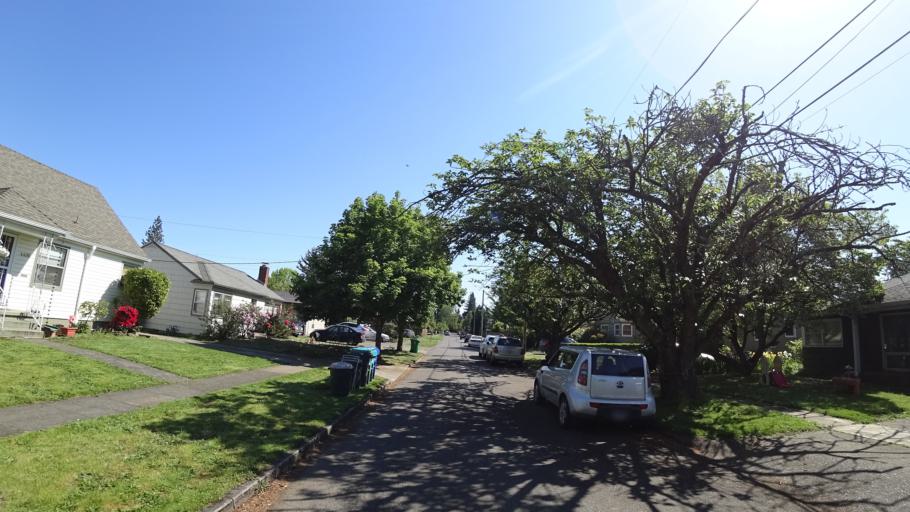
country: US
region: Oregon
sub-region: Multnomah County
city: Lents
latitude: 45.4913
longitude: -122.6119
